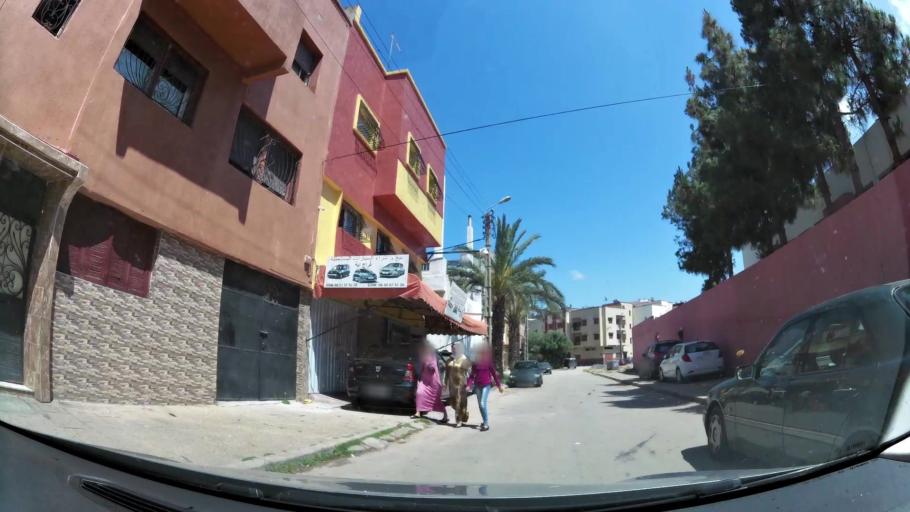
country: MA
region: Rabat-Sale-Zemmour-Zaer
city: Sale
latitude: 34.0459
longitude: -6.7920
